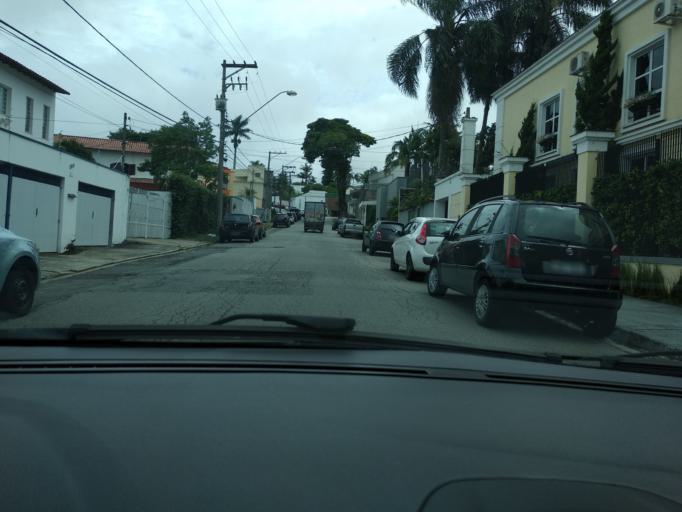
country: BR
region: Sao Paulo
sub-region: Mogi das Cruzes
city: Mogi das Cruzes
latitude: -23.5220
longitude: -46.1752
